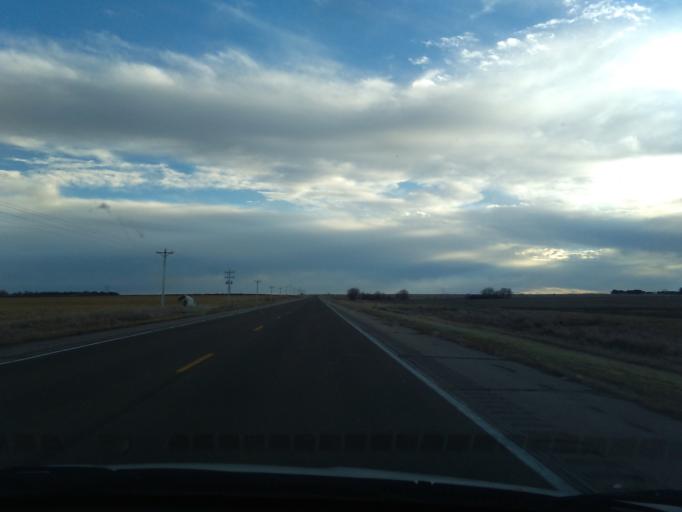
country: US
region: Nebraska
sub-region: Phelps County
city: Holdrege
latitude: 40.3918
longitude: -99.3700
